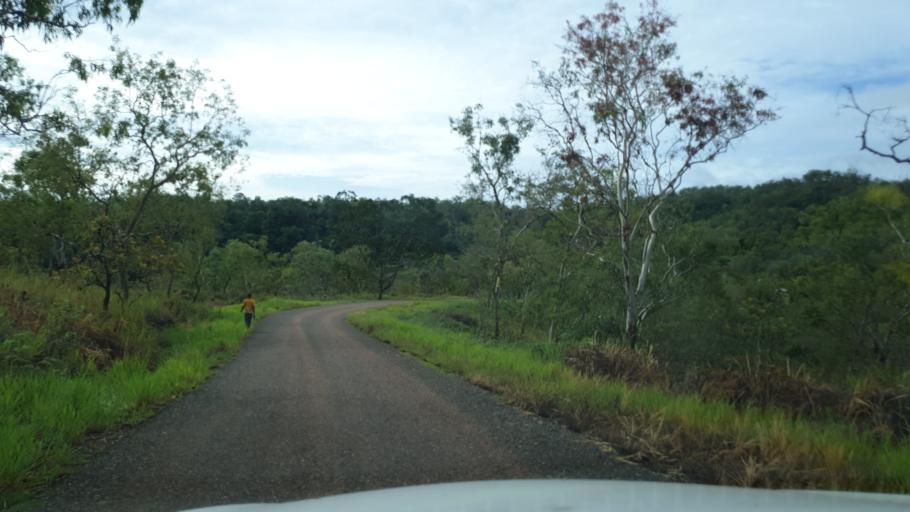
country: PG
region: National Capital
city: Port Moresby
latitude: -9.4332
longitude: 147.3963
